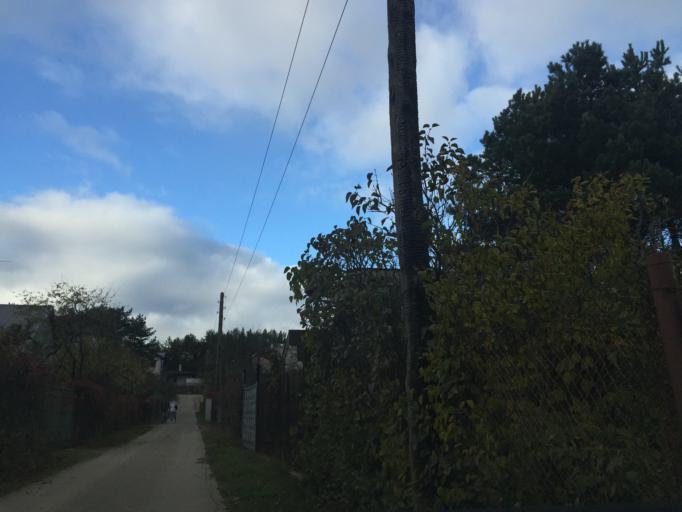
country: LV
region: Carnikava
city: Carnikava
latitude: 57.1523
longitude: 24.2820
